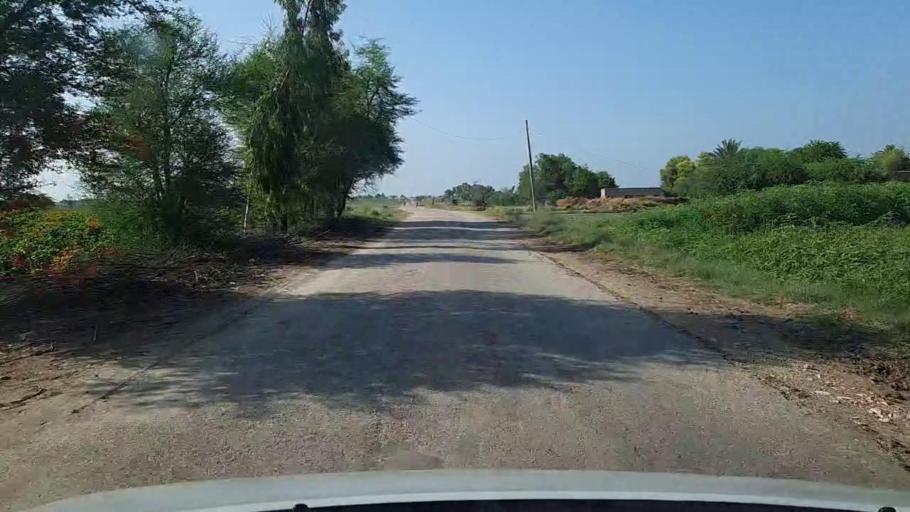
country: PK
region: Sindh
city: Kandiaro
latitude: 27.0597
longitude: 68.3165
